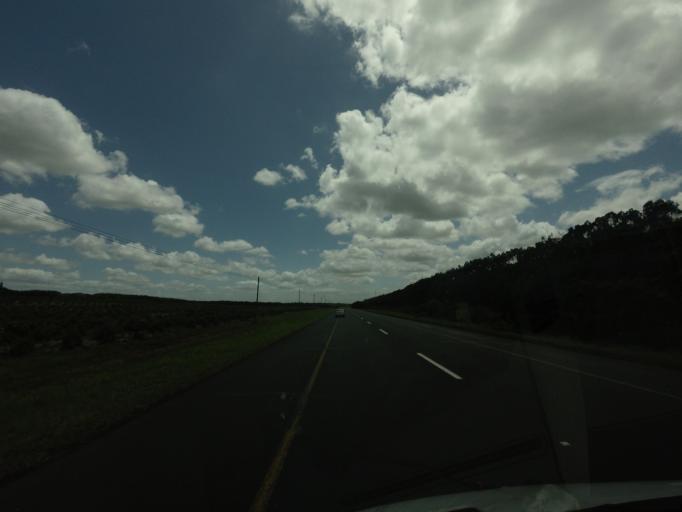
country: ZA
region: KwaZulu-Natal
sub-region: uThungulu District Municipality
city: KwaMbonambi
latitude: -28.5595
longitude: 32.1163
